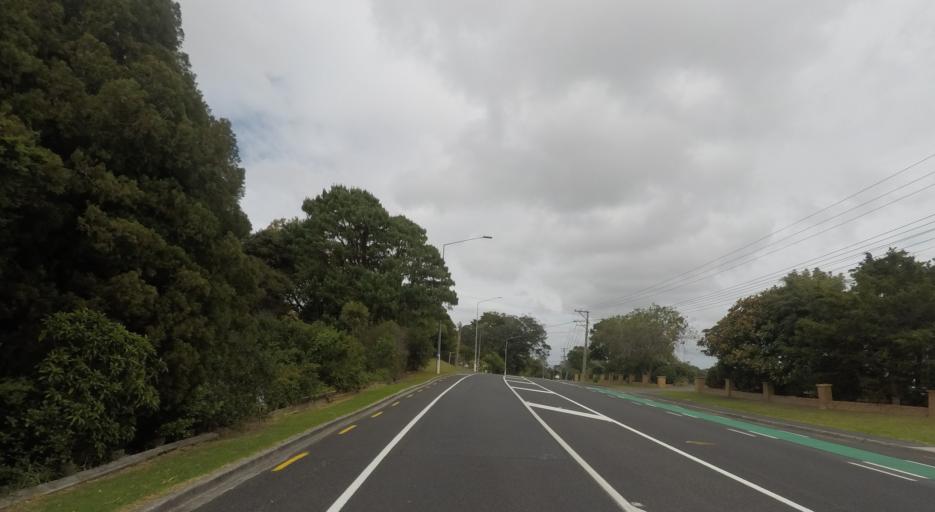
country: NZ
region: Auckland
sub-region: Auckland
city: North Shore
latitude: -36.7732
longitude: 174.6933
